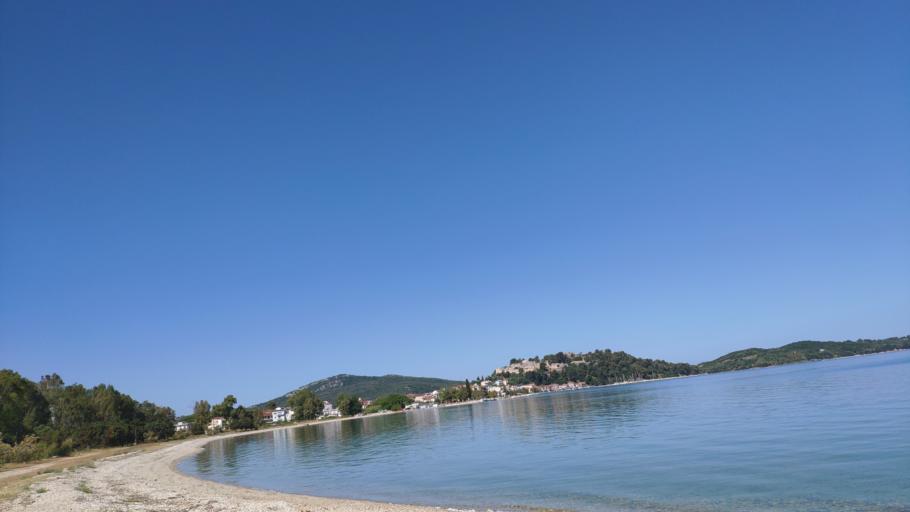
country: GR
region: West Greece
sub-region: Nomos Aitolias kai Akarnanias
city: Vonitsa
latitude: 38.9222
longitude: 20.9003
